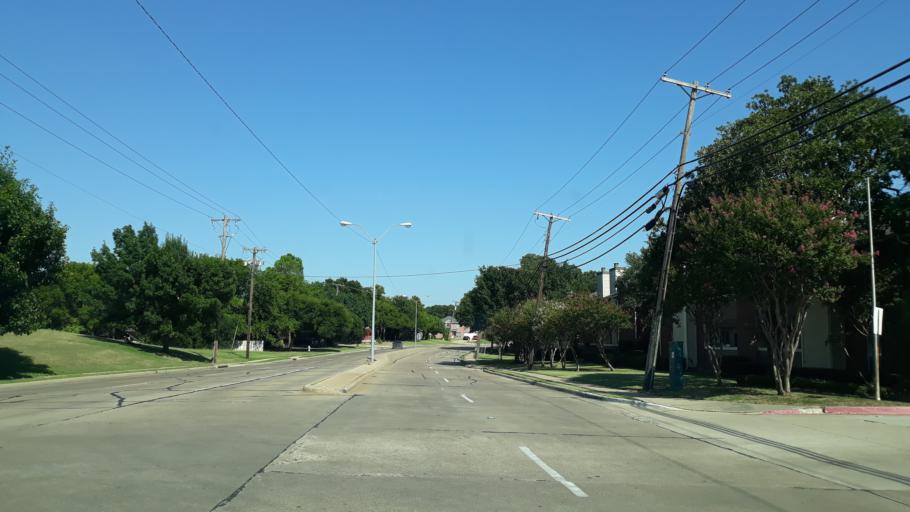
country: US
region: Texas
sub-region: Dallas County
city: Irving
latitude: 32.8325
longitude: -97.0074
